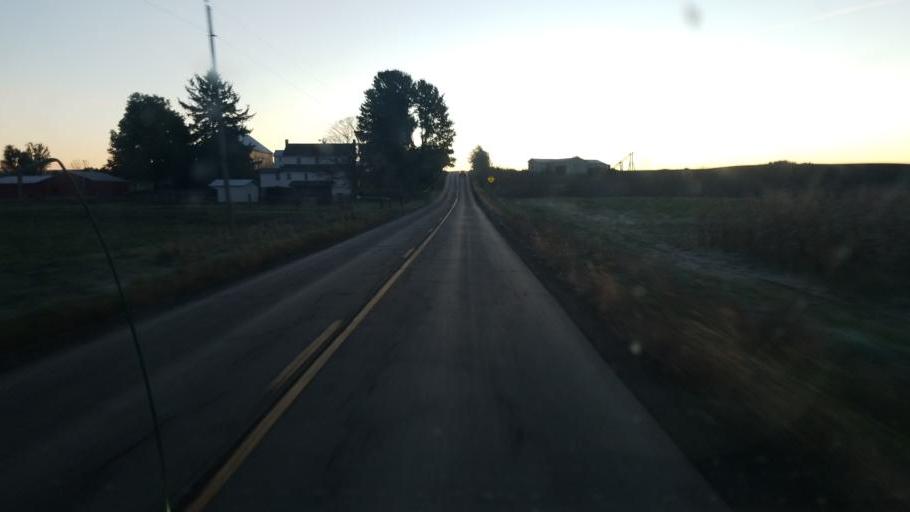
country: US
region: Ohio
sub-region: Wayne County
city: Apple Creek
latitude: 40.7410
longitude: -81.7934
